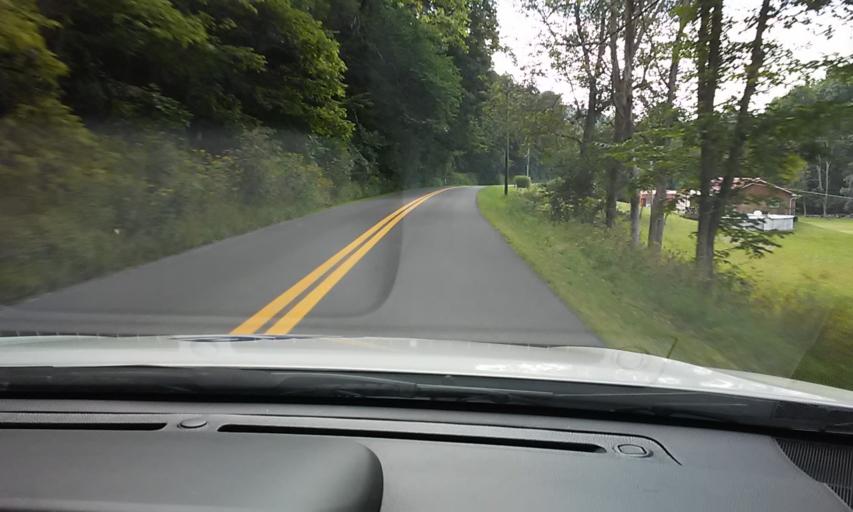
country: US
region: West Virginia
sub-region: Marion County
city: Mannington
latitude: 39.6527
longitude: -80.2998
